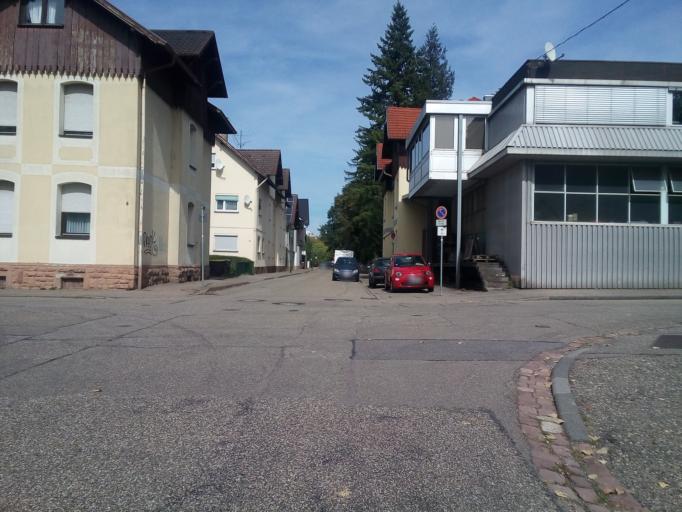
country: DE
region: Baden-Wuerttemberg
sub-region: Karlsruhe Region
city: Sinzheim
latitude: 48.7833
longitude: 8.1874
